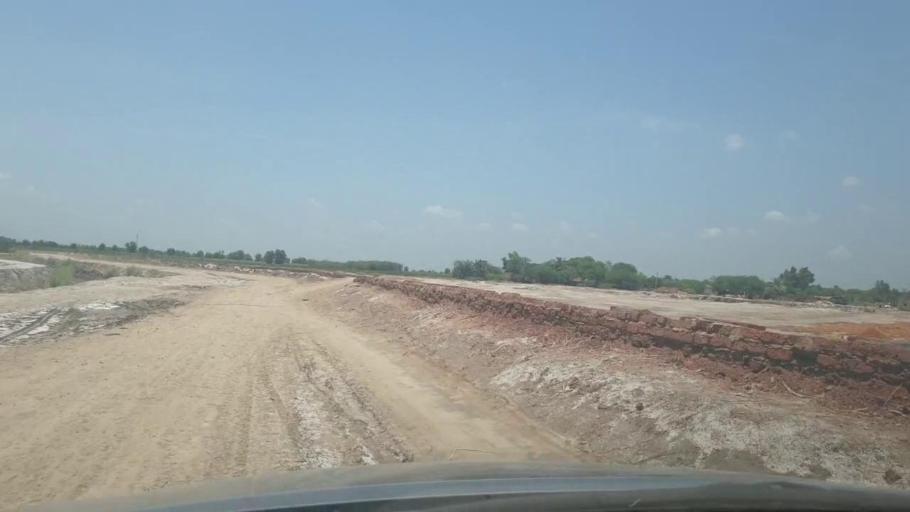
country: PK
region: Sindh
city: Kot Diji
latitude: 27.3870
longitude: 68.6968
